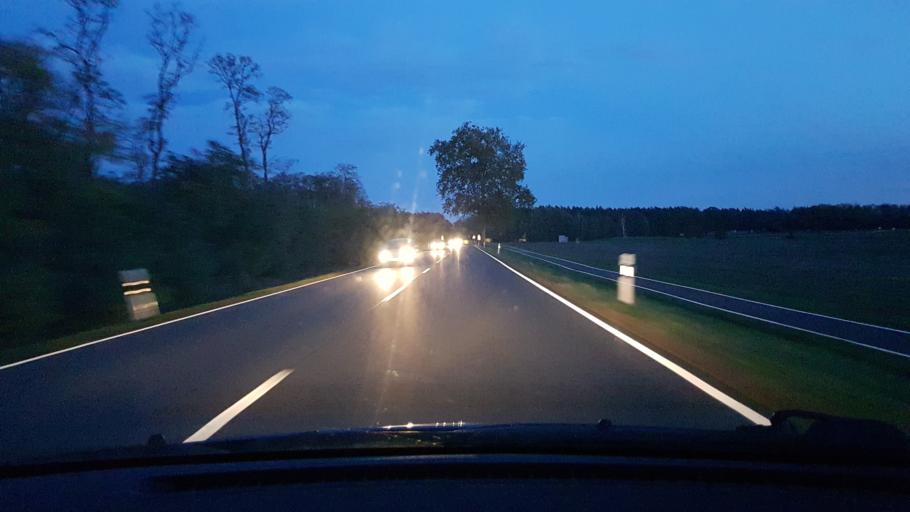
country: DE
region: Saxony-Anhalt
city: Rodleben
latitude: 51.9279
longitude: 12.1499
